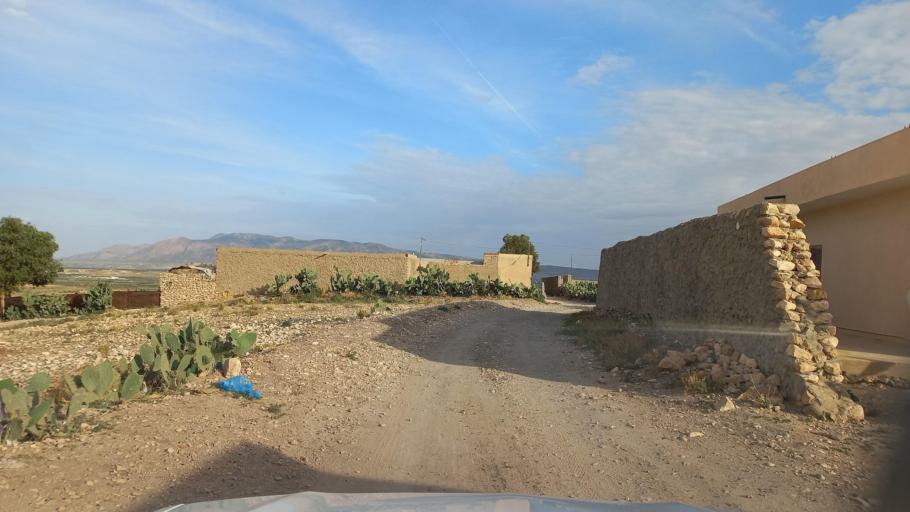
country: TN
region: Al Qasrayn
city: Sbiba
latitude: 35.4547
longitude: 9.0850
